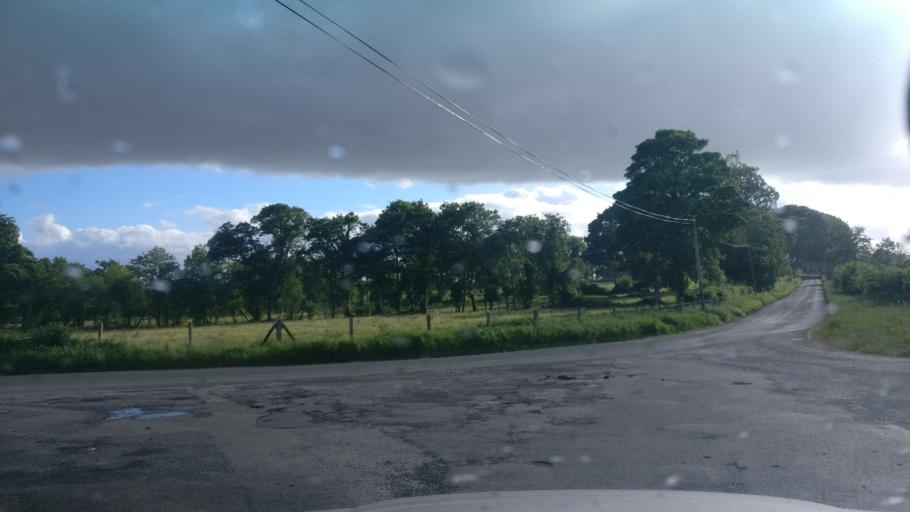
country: IE
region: Connaught
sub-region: County Galway
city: Ballinasloe
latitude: 53.2279
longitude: -8.2275
